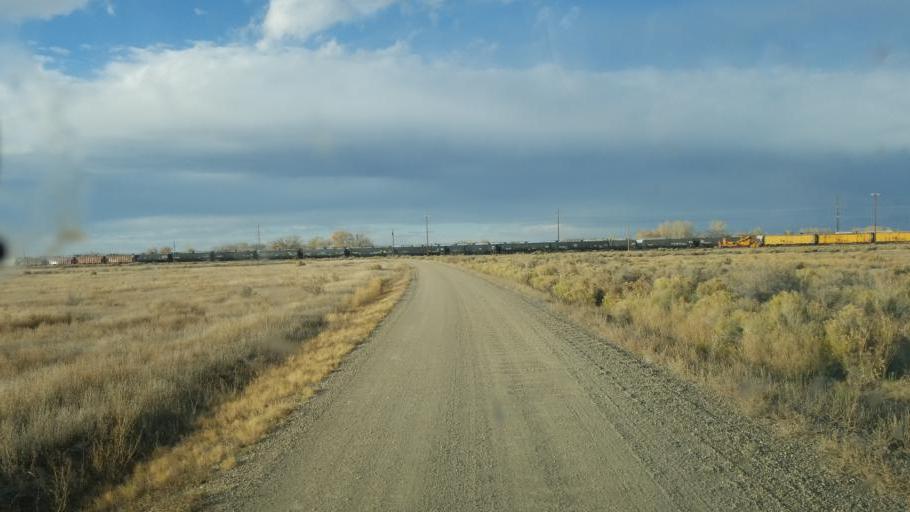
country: US
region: Colorado
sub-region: Alamosa County
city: Alamosa East
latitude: 37.4628
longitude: -105.8336
